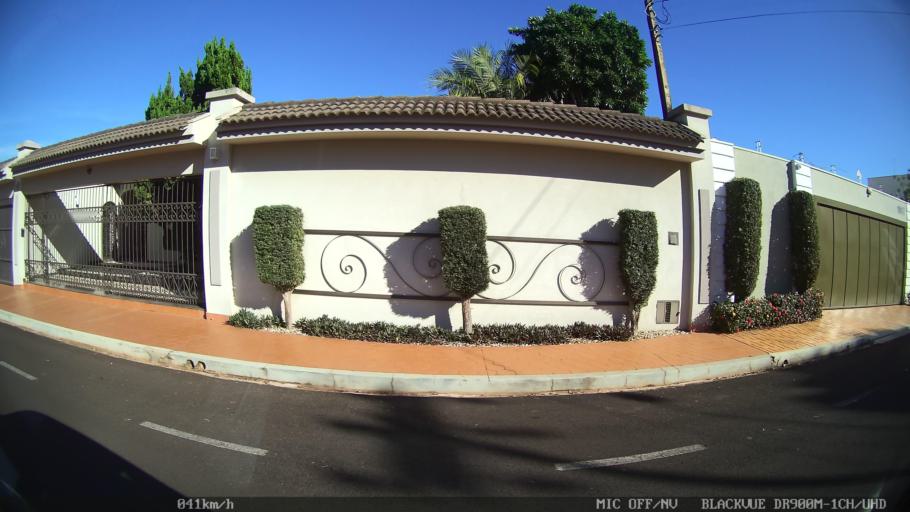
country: BR
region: Sao Paulo
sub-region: Franca
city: Franca
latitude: -20.5437
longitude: -47.4055
